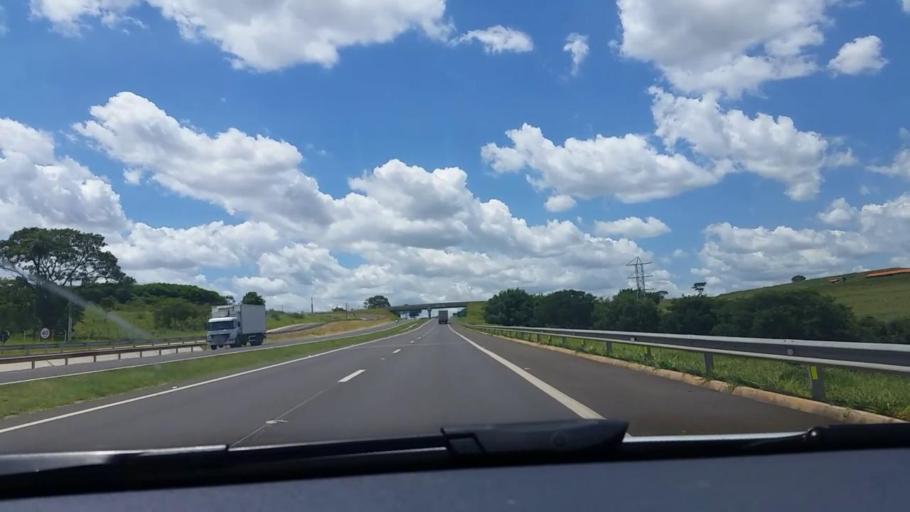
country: BR
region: Sao Paulo
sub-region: Bauru
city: Bauru
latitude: -22.4017
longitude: -49.0916
